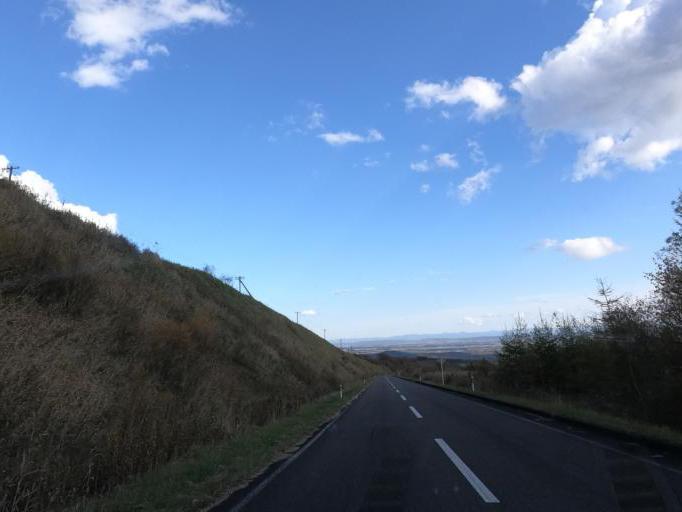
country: JP
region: Hokkaido
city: Otofuke
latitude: 43.2933
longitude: 143.1920
